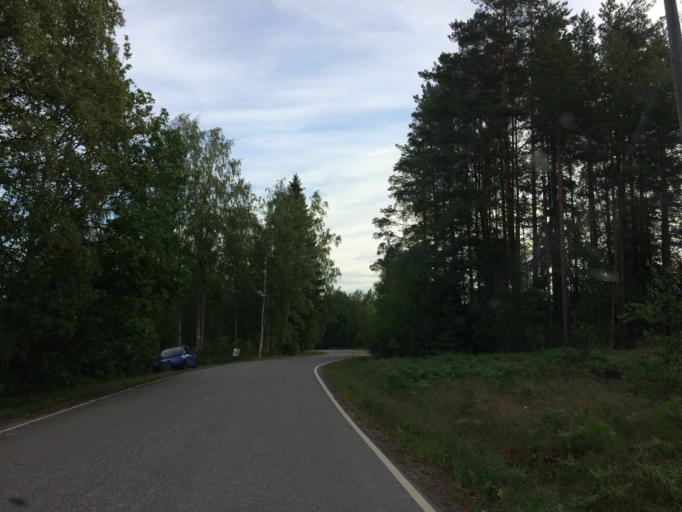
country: FI
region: Haeme
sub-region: Haemeenlinna
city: Janakkala
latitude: 60.8666
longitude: 24.5531
